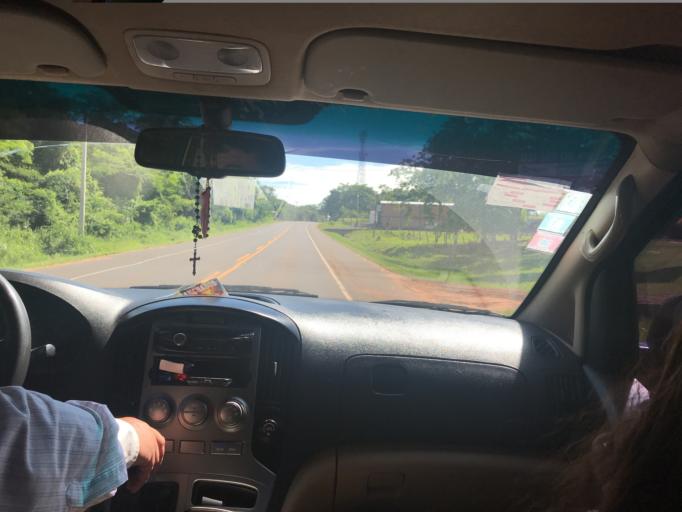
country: PY
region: San Pedro
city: Union
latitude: -24.6807
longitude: -56.4661
